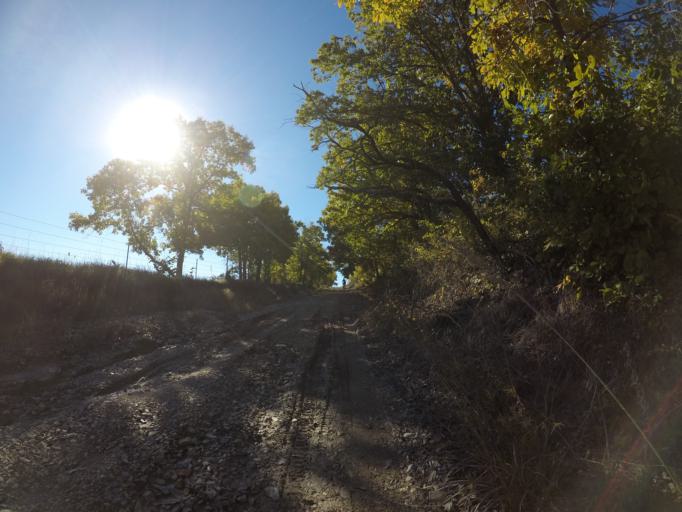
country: US
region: Kansas
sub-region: Wabaunsee County
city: Alma
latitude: 38.8849
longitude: -96.3908
